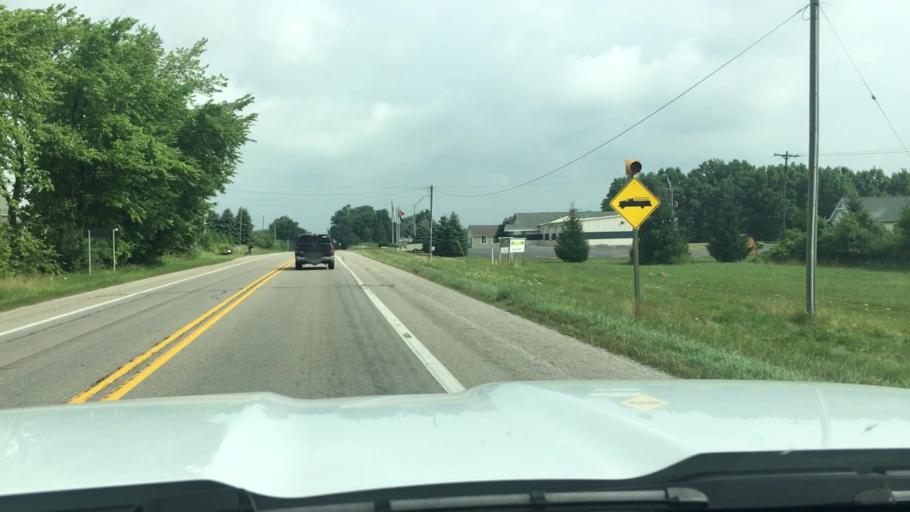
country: US
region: Michigan
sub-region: Lapeer County
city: Imlay City
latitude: 43.1038
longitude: -83.0720
